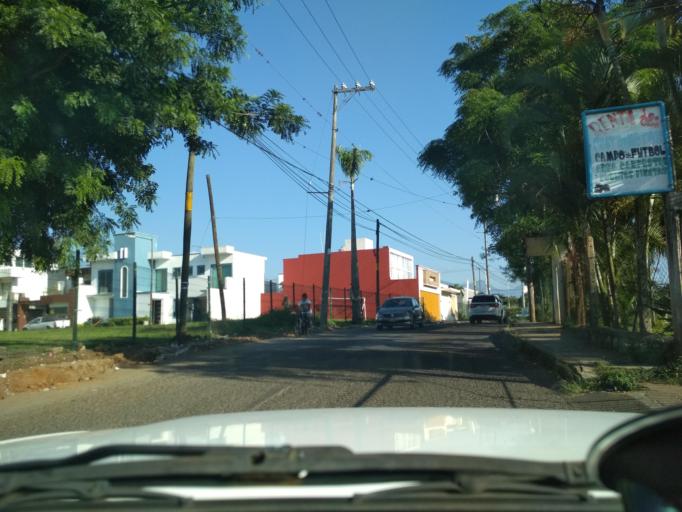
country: MX
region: Veracruz
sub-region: Fortin
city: Fraccionamiento Villas de la Llave
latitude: 18.9139
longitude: -96.9876
